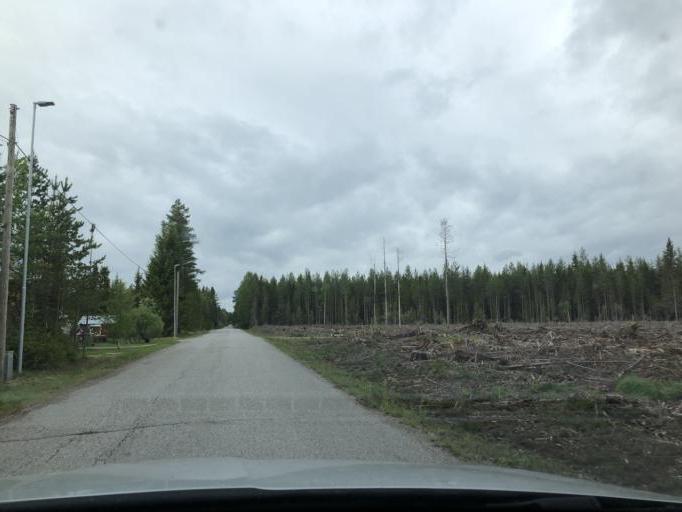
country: SE
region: Norrbotten
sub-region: Pitea Kommun
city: Roknas
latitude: 65.3787
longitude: 21.2769
